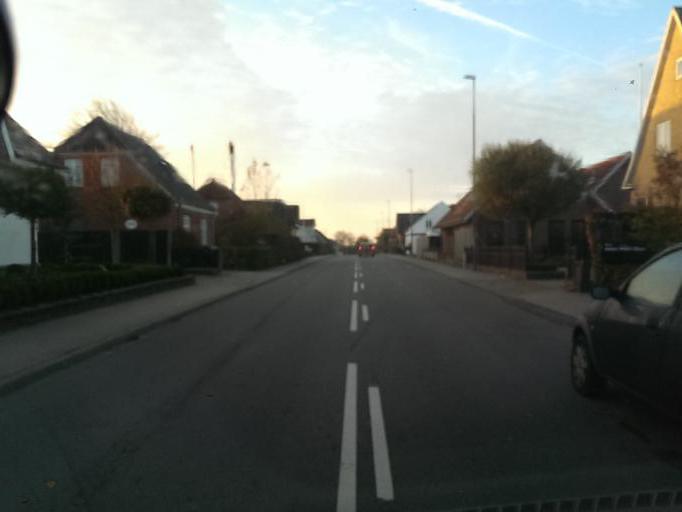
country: DK
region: South Denmark
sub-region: Esbjerg Kommune
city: Tjaereborg
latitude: 55.4661
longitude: 8.5765
